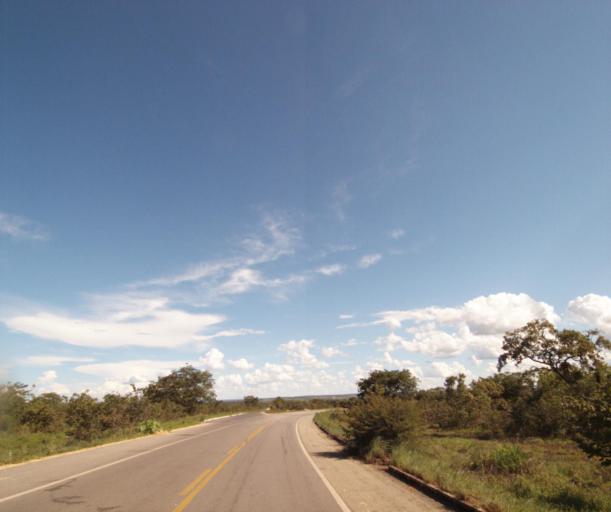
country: BR
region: Bahia
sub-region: Correntina
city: Correntina
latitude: -13.3090
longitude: -44.6421
